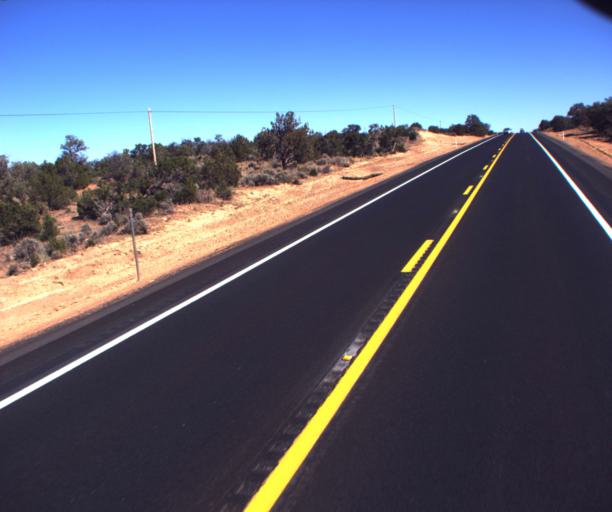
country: US
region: Arizona
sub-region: Apache County
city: Ganado
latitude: 35.7190
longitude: -109.3793
